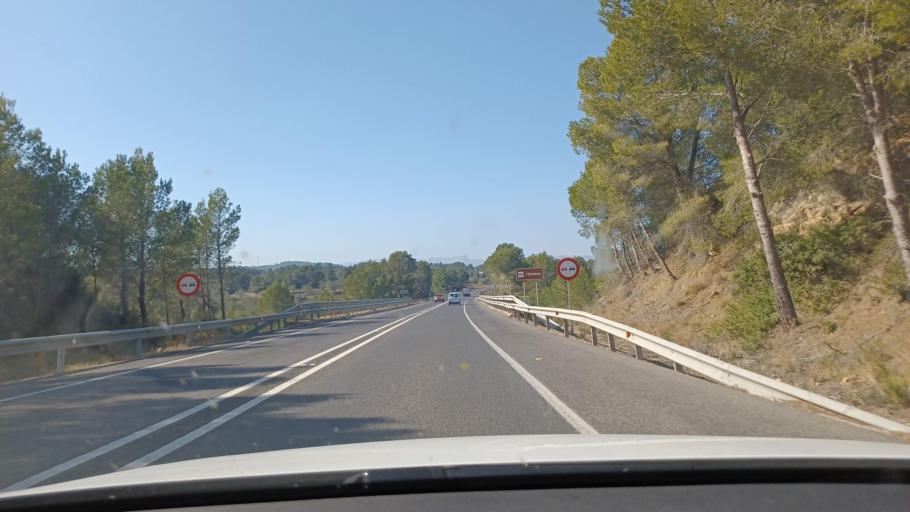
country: ES
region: Catalonia
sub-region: Provincia de Tarragona
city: l'Ametlla de Mar
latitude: 40.8948
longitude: 0.7641
